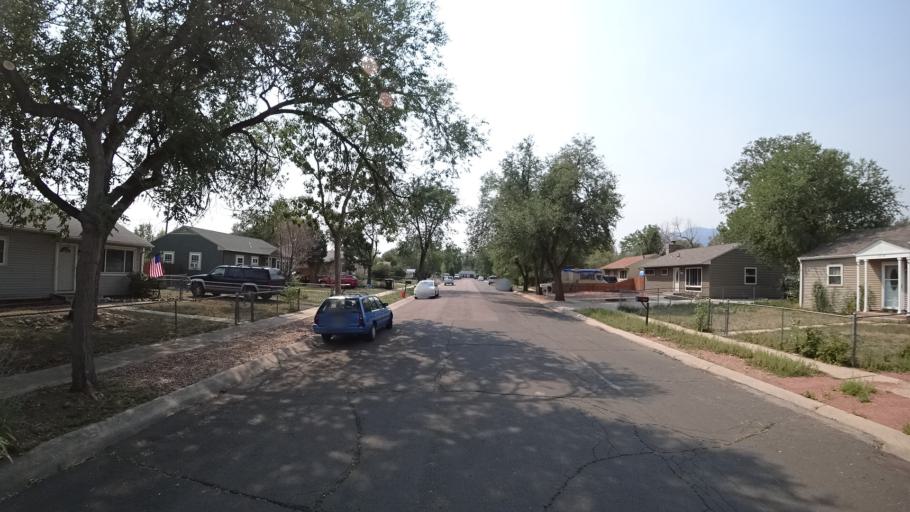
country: US
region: Colorado
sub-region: El Paso County
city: Colorado Springs
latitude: 38.8056
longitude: -104.8103
